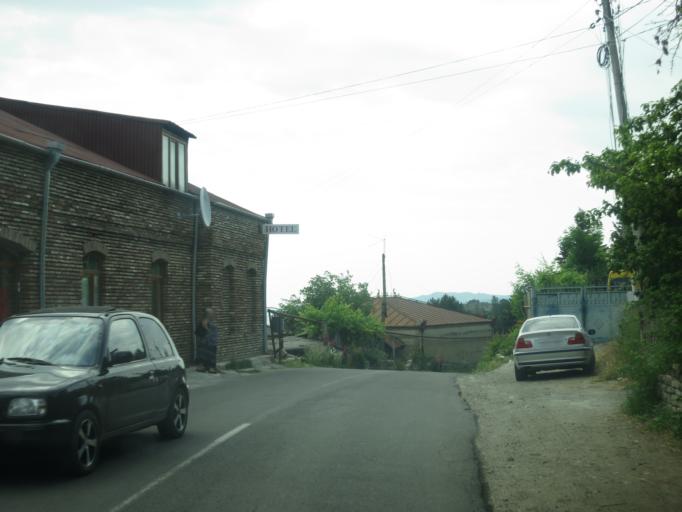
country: GE
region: Kakheti
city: Sighnaghi
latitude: 41.6133
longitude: 45.9234
